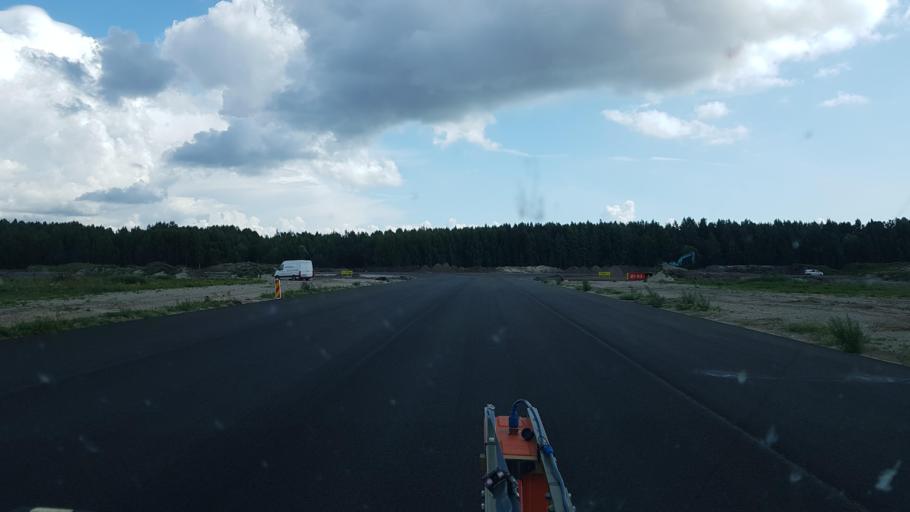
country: EE
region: Paernumaa
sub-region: Sauga vald
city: Sauga
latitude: 58.4200
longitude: 24.4692
